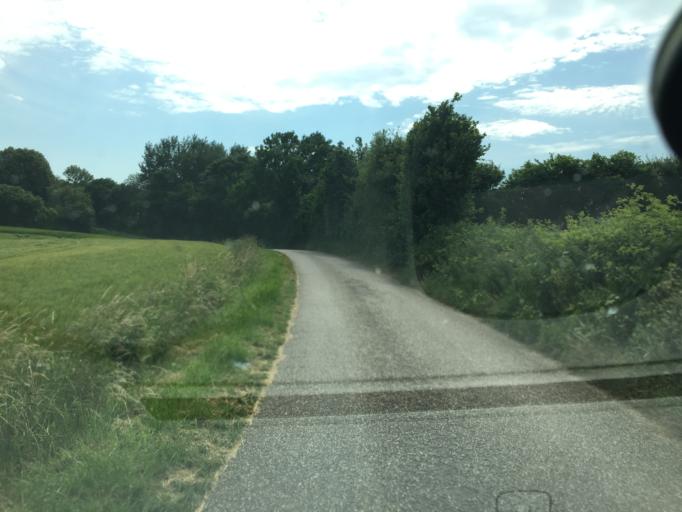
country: DK
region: South Denmark
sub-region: Sonderborg Kommune
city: Dybbol
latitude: 54.9421
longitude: 9.7408
